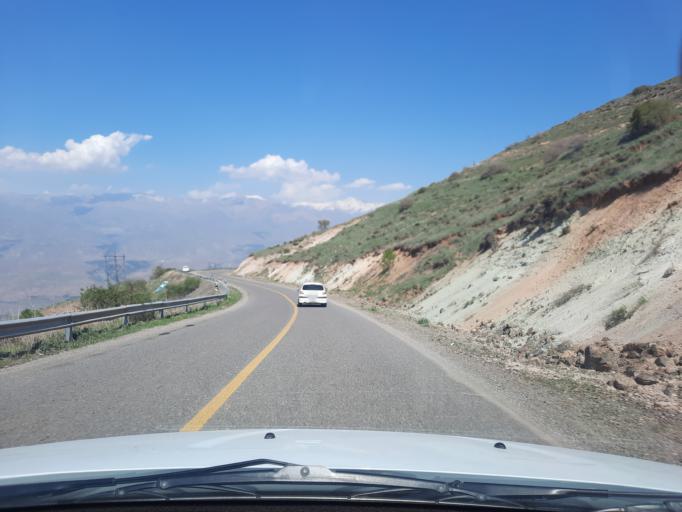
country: IR
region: Qazvin
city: Qazvin
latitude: 36.4119
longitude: 50.2364
